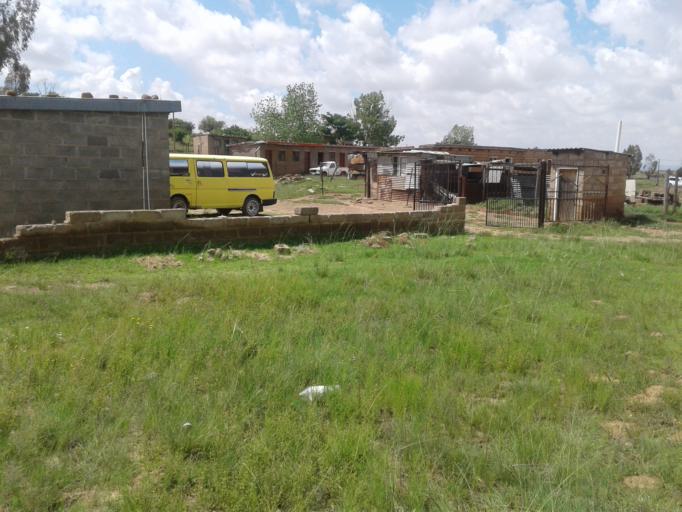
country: LS
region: Mafeteng
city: Mafeteng
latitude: -29.7553
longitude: 27.1127
